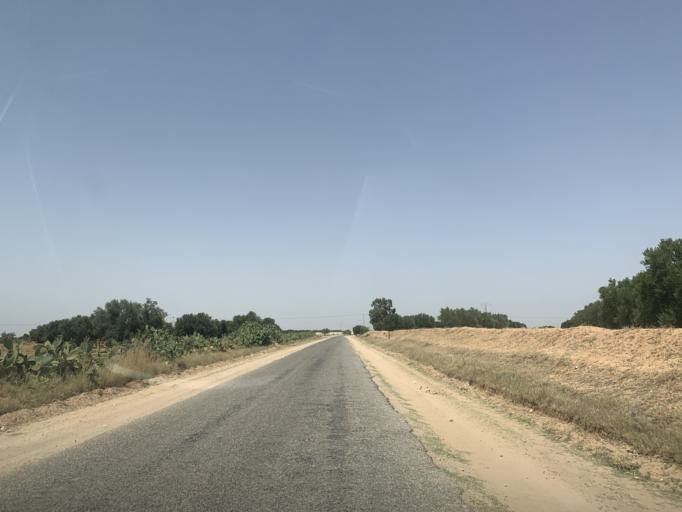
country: TN
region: Al Mahdiyah
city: Shurban
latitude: 35.1791
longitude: 10.2354
